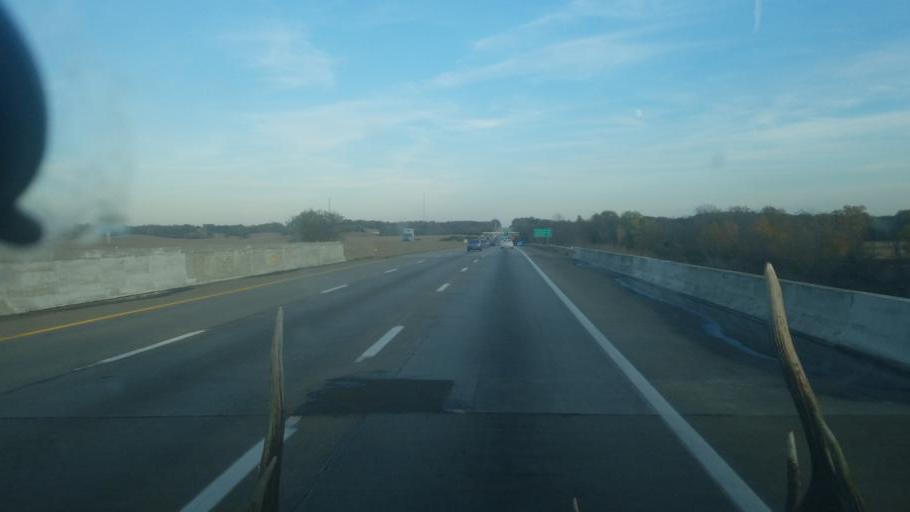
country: US
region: Ohio
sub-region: Licking County
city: Harbor Hills
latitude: 39.9457
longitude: -82.4391
